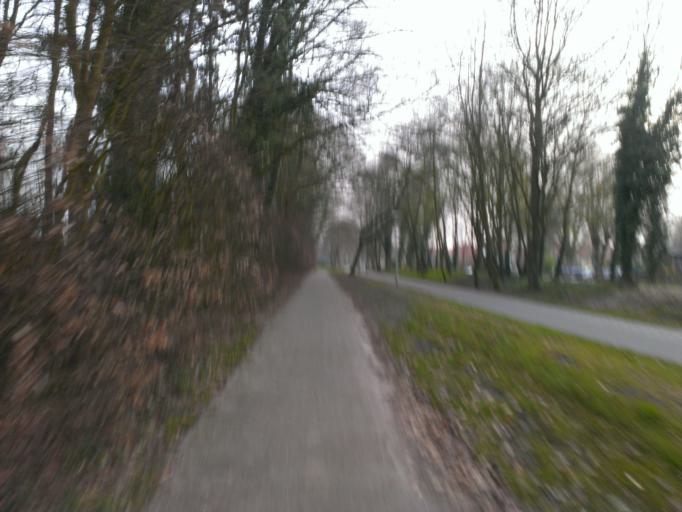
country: NL
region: Gelderland
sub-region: Gemeente Heerde
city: Heerde
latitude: 52.3848
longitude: 6.0321
